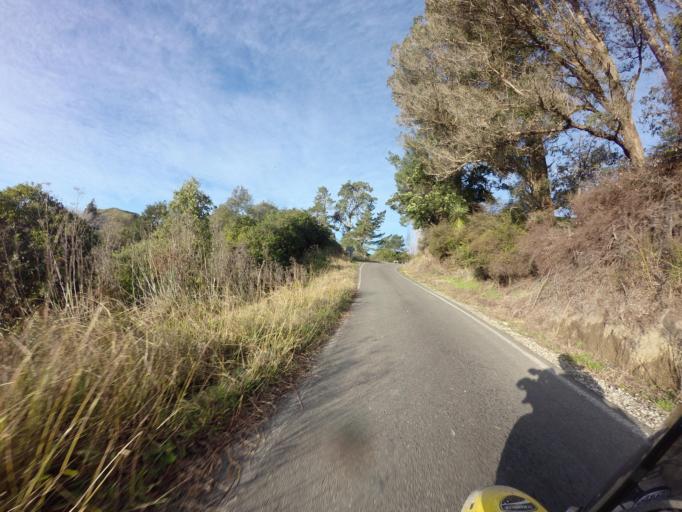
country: NZ
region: Hawke's Bay
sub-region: Wairoa District
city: Wairoa
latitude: -38.7346
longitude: 177.5921
